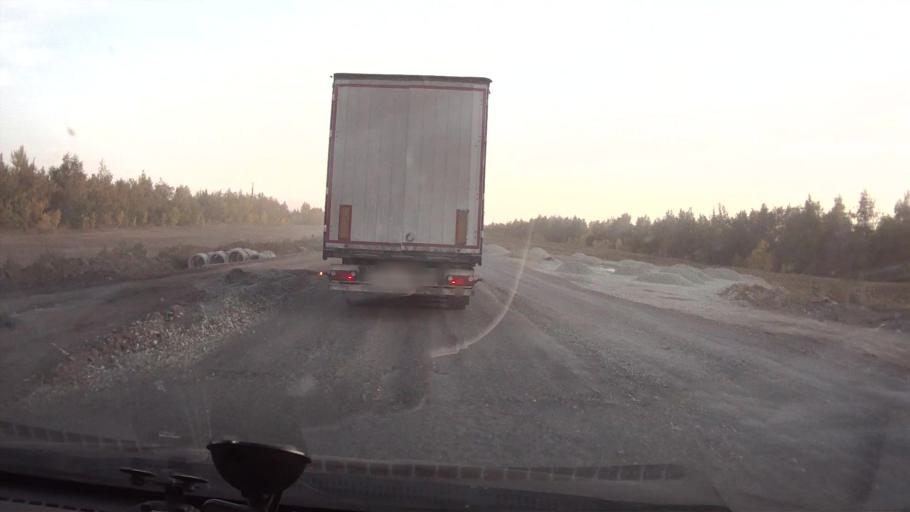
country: RU
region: Saratov
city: Kamenskiy
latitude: 50.9266
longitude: 45.5992
